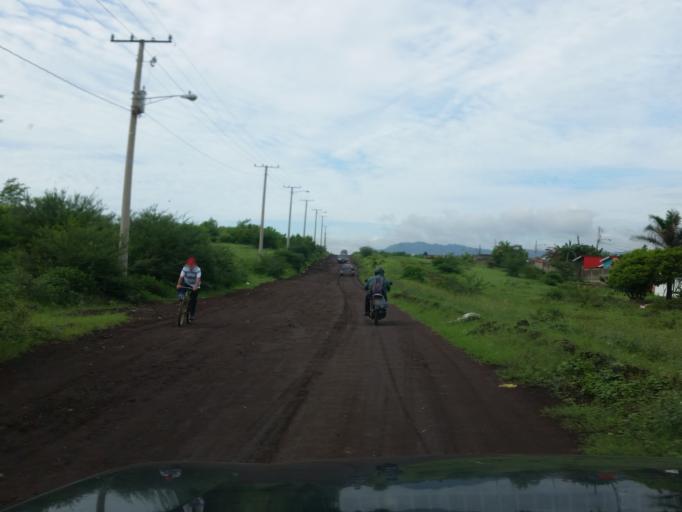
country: NI
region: Managua
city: Managua
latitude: 12.1056
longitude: -86.2047
